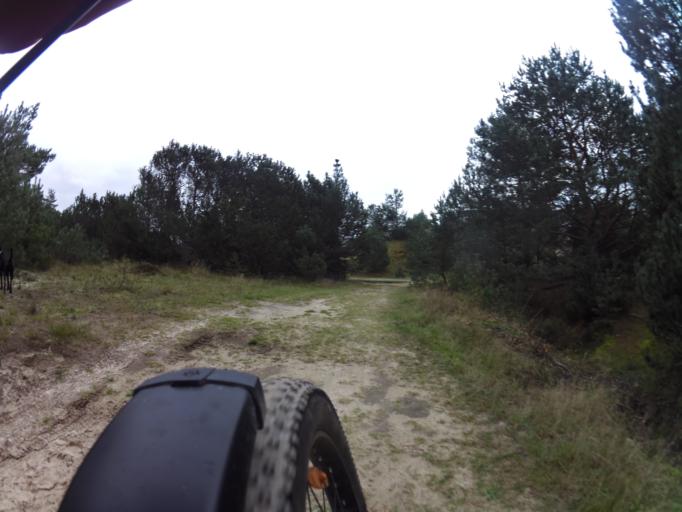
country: PL
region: Pomeranian Voivodeship
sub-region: Powiat leborski
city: Leba
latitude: 54.7698
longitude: 17.5930
